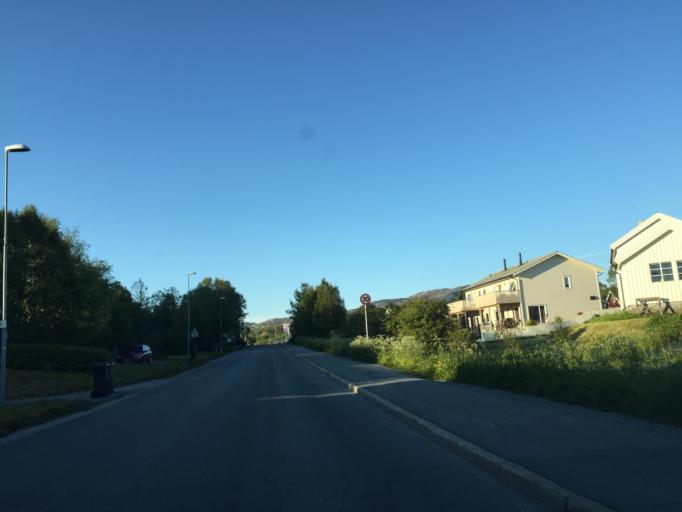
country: NO
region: Nordland
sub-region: Bodo
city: Loding
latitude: 67.2991
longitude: 14.7335
